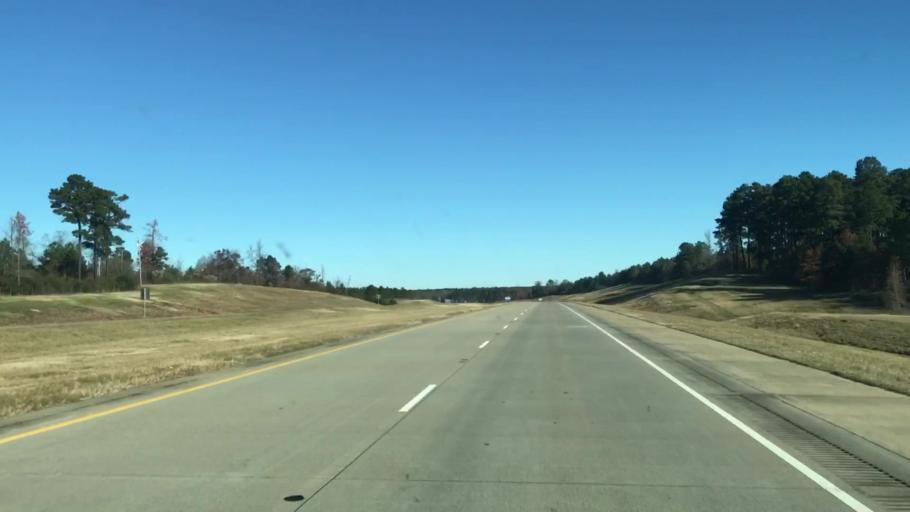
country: US
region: Louisiana
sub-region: Caddo Parish
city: Vivian
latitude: 33.0120
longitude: -93.9033
